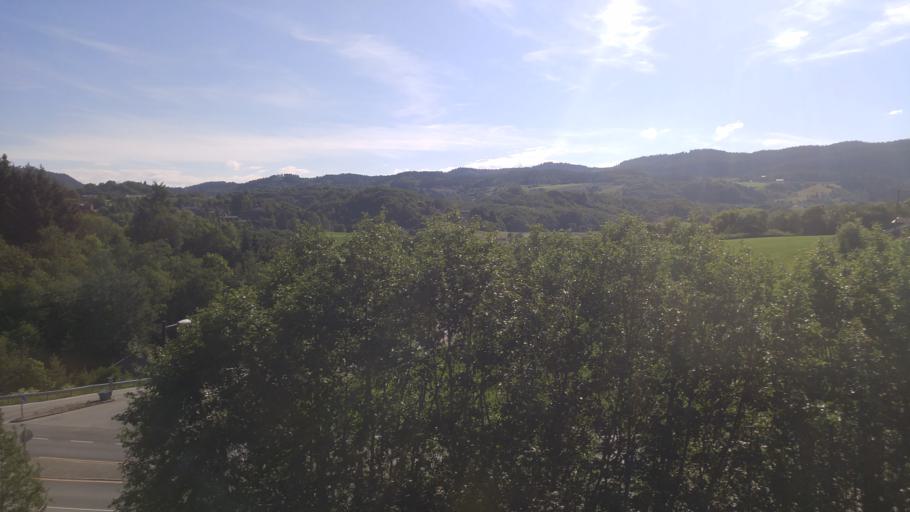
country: NO
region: Sor-Trondelag
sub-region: Melhus
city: Melhus
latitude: 63.2286
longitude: 10.2866
